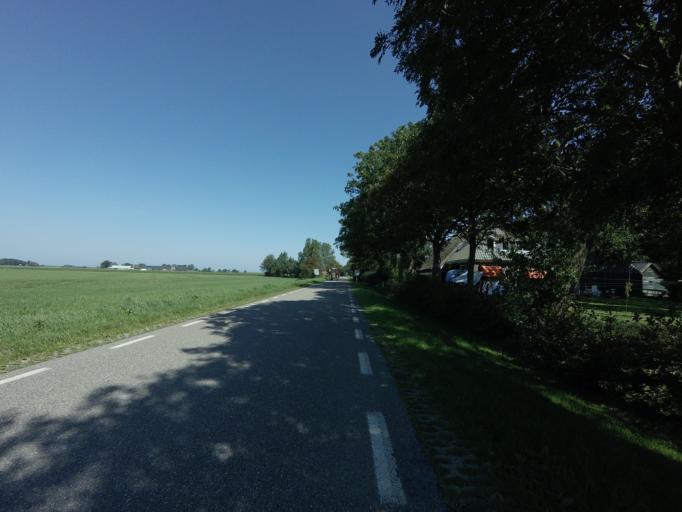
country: NL
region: Friesland
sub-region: Gemeente Dongeradeel
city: Ternaard
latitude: 53.3750
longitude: 5.9995
